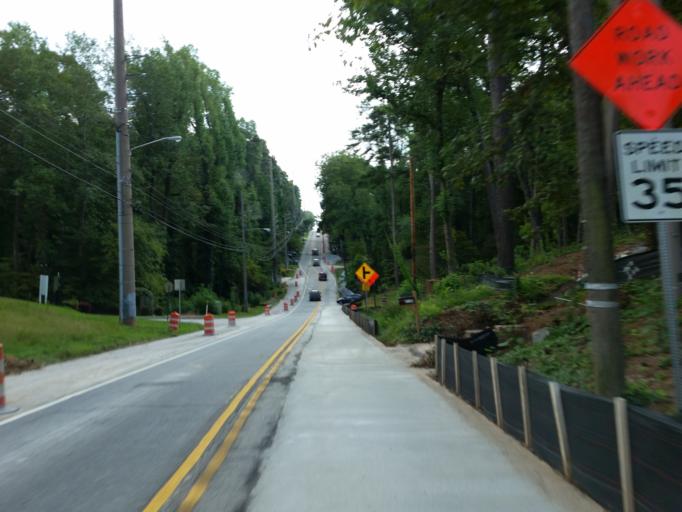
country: US
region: Georgia
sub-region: Fulton County
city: Atlanta
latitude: 33.8140
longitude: -84.4078
